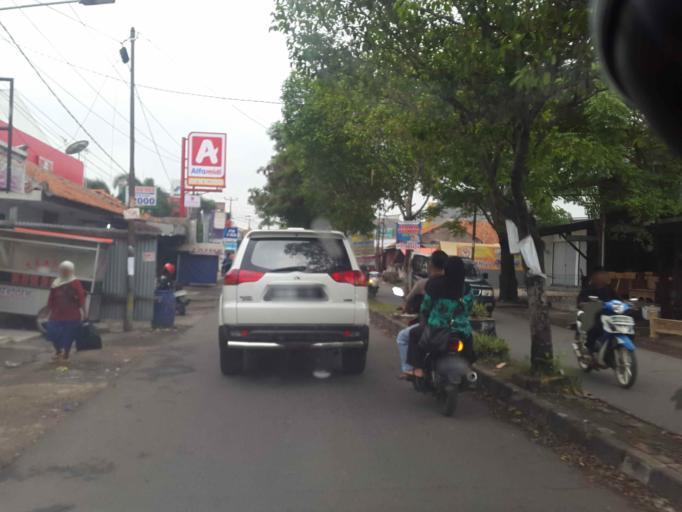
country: ID
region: West Java
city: Bekasi
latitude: -6.2428
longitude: 107.0267
